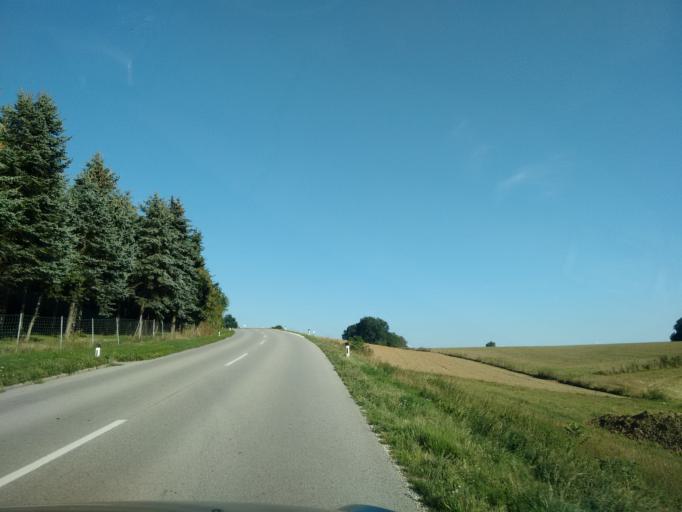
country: AT
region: Upper Austria
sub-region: Wels-Land
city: Marchtrenk
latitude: 48.1476
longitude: 14.1851
